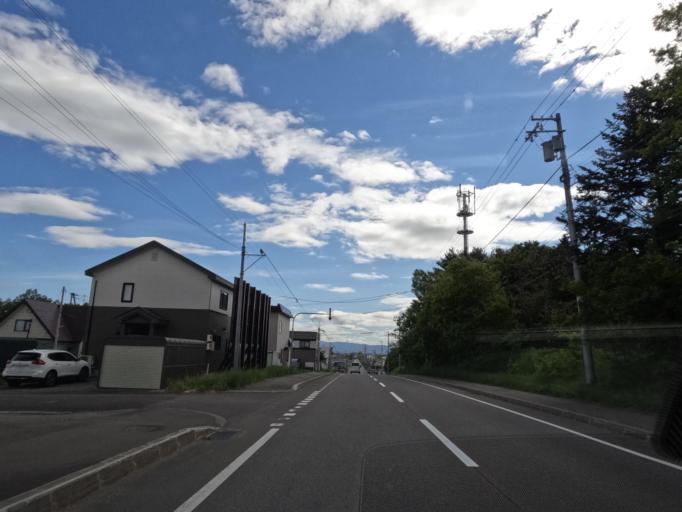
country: JP
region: Hokkaido
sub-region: Asahikawa-shi
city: Asahikawa
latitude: 43.8288
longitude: 142.5264
